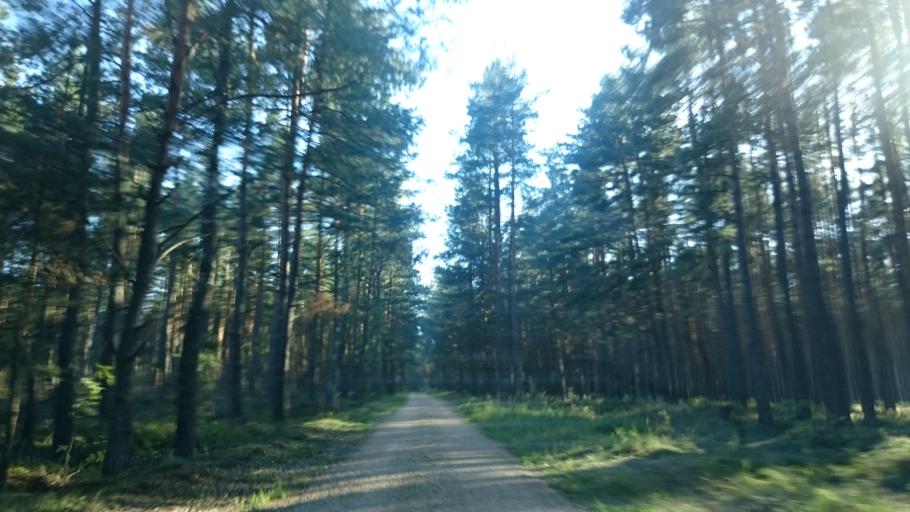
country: LV
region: Carnikava
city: Carnikava
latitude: 57.1083
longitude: 24.2372
